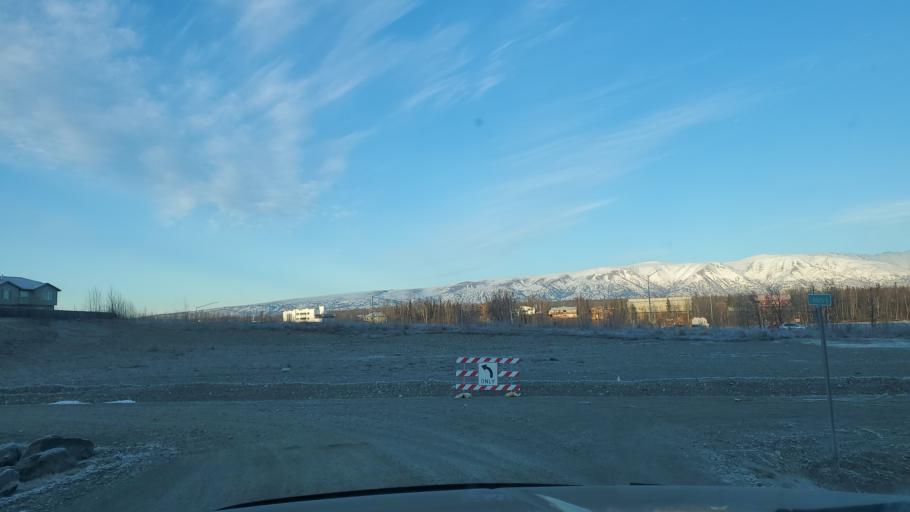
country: US
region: Alaska
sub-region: Matanuska-Susitna Borough
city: Wasilla
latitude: 61.5782
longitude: -149.4237
